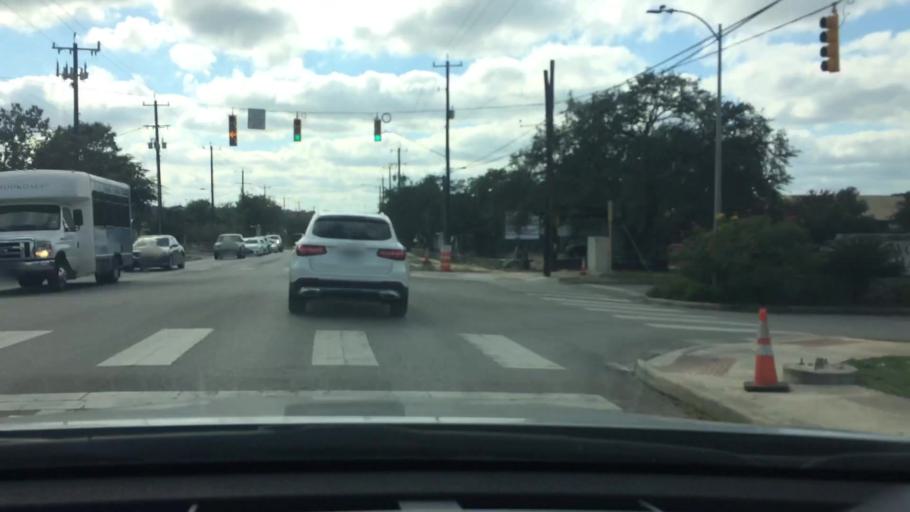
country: US
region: Texas
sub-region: Bexar County
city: Shavano Park
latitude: 29.5710
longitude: -98.5737
